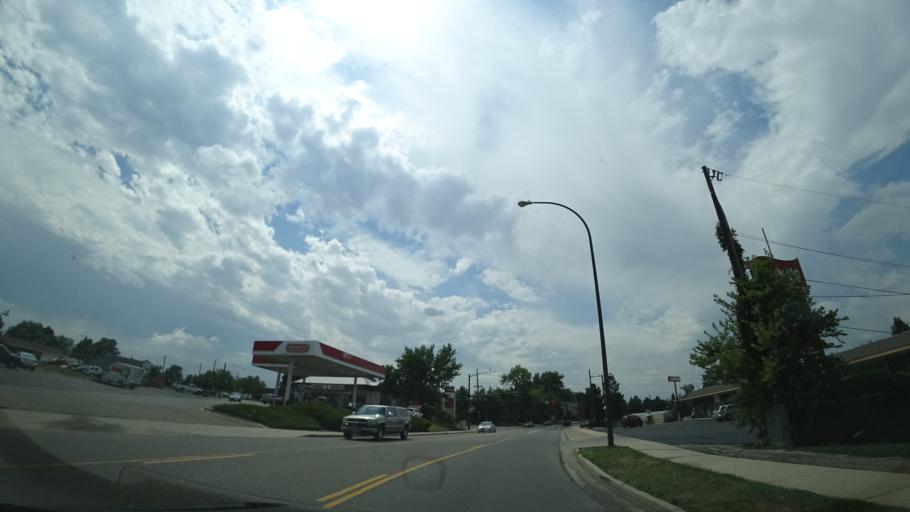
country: US
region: Colorado
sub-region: Jefferson County
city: Lakewood
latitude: 39.6960
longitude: -105.0710
